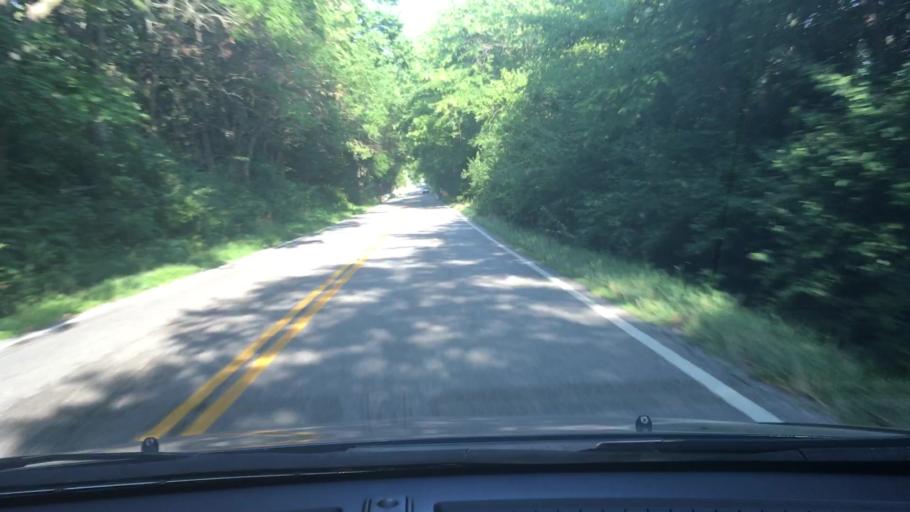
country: US
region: Missouri
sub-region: Jackson County
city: Lees Summit
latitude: 38.8908
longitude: -94.4360
